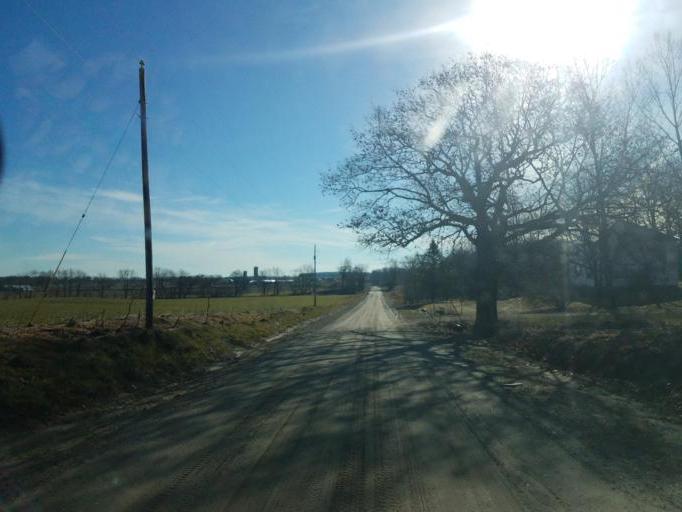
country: US
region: Michigan
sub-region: Montcalm County
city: Edmore
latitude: 43.4949
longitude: -85.0738
